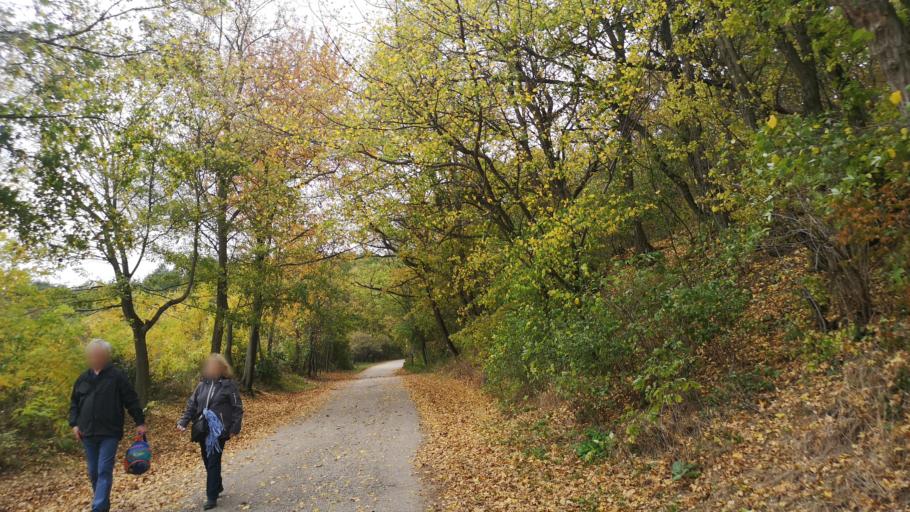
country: SK
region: Nitriansky
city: Cachtice
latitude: 48.7171
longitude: 17.7695
